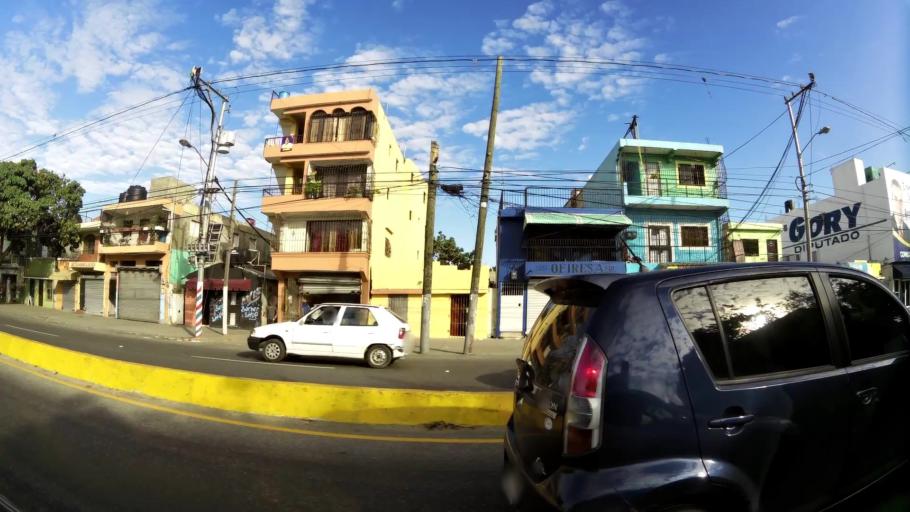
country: DO
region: Nacional
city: Ensanche Luperon
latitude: 18.4946
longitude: -69.8975
